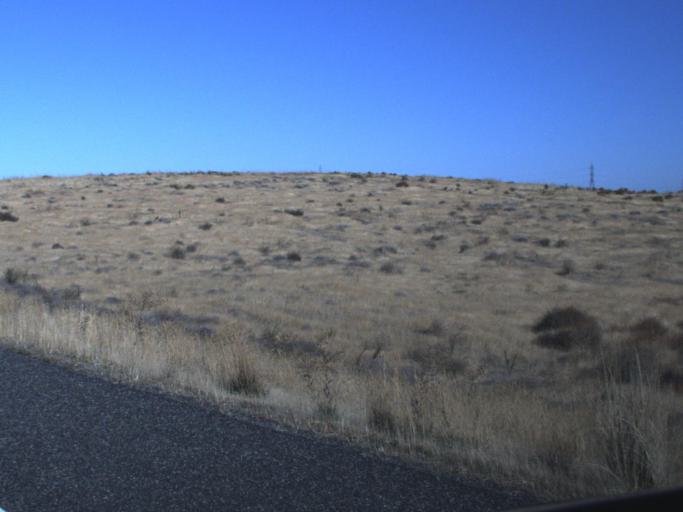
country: US
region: Washington
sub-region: Benton County
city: West Richland
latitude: 46.3521
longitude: -119.3656
